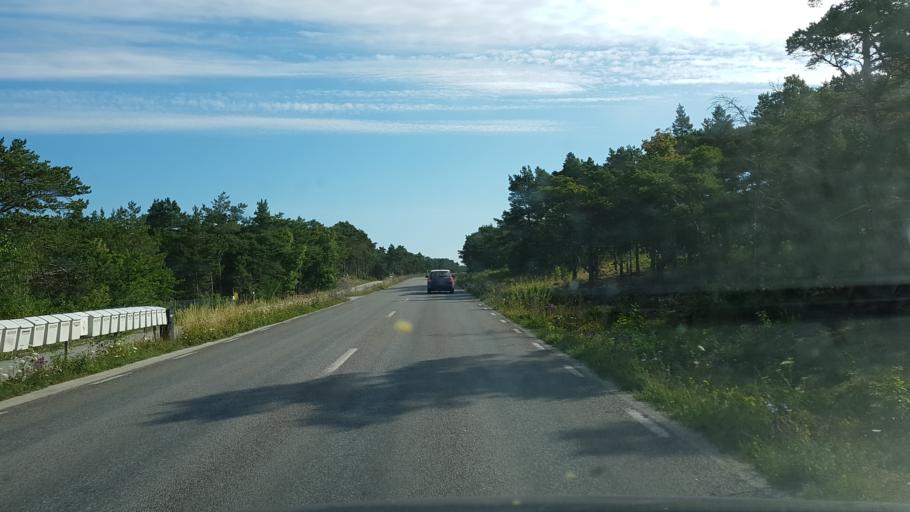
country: SE
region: Gotland
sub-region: Gotland
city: Visby
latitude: 57.7172
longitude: 18.3894
